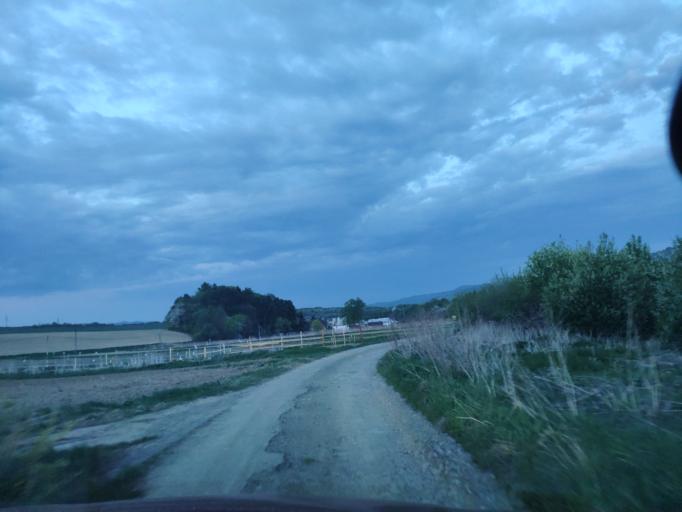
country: SK
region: Presovsky
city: Lipany
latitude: 49.1783
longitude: 20.8516
